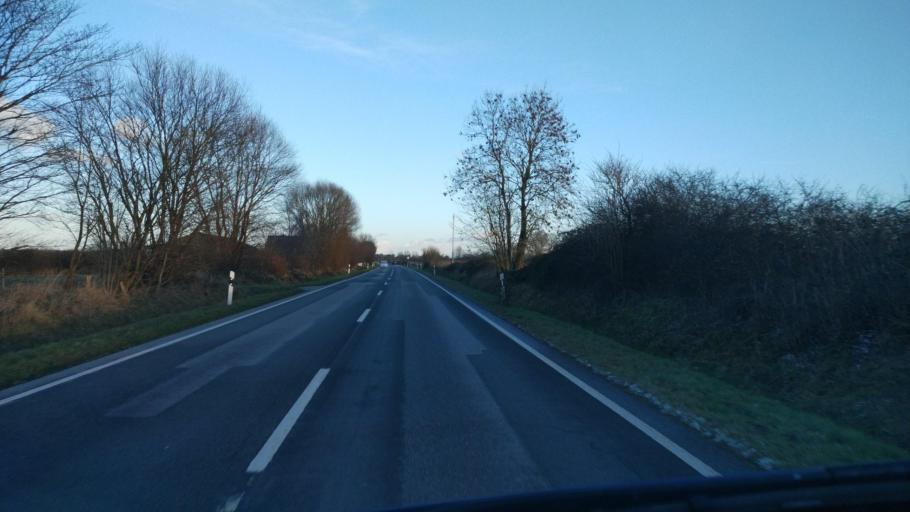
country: DE
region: Schleswig-Holstein
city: Wittbek
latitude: 54.4619
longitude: 9.1966
